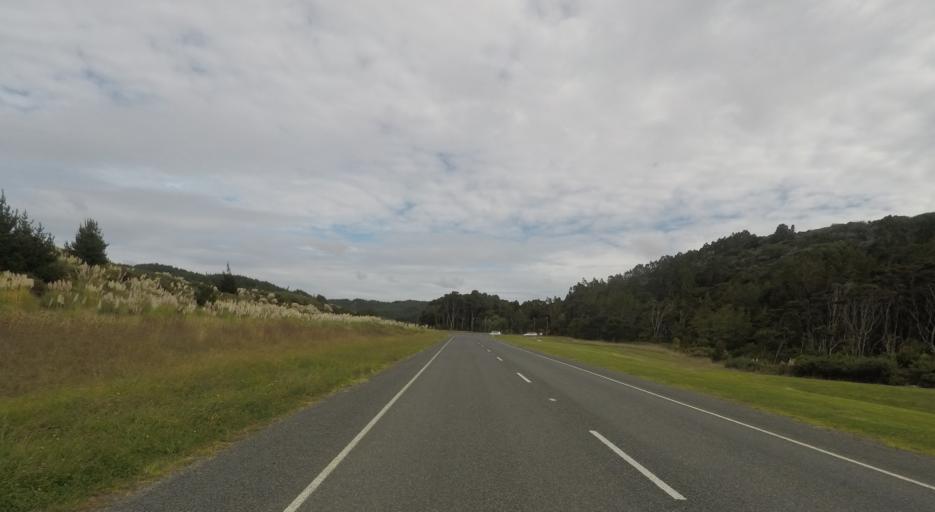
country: NZ
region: Auckland
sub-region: Auckland
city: Rothesay Bay
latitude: -36.6535
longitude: 174.7198
